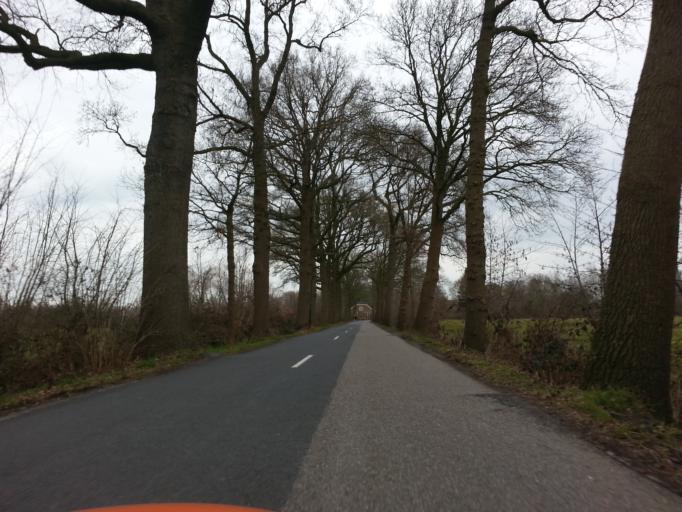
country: NL
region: Utrecht
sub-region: Gemeente Leusden
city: Leusden
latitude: 52.1109
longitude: 5.4196
